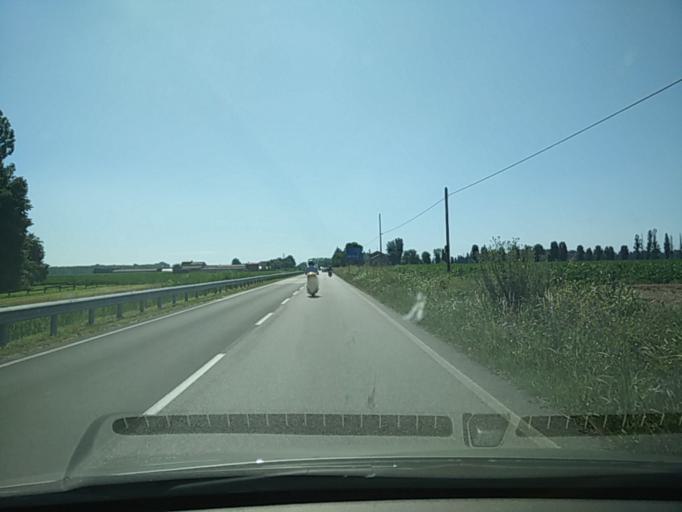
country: IT
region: Veneto
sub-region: Provincia di Venezia
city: San Giorgio di Livenza
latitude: 45.6227
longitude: 12.7950
